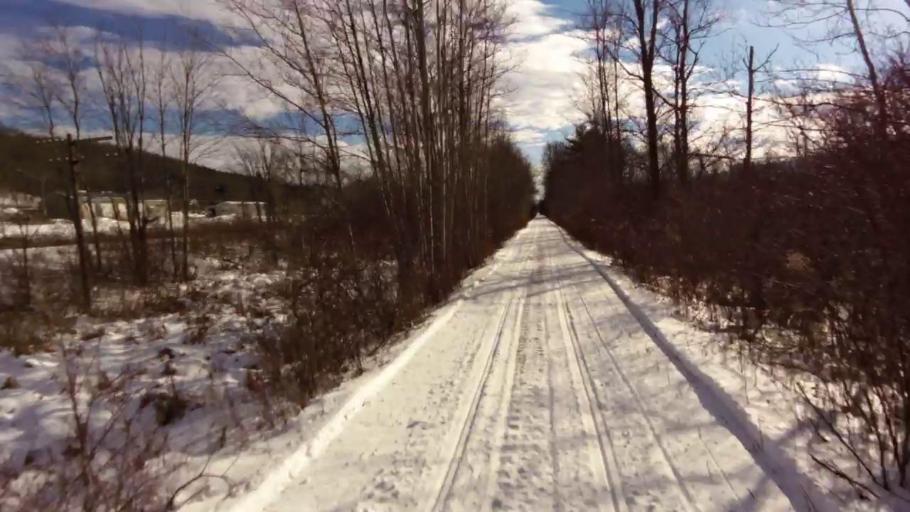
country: US
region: Pennsylvania
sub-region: McKean County
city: Foster Brook
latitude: 42.0450
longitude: -78.6351
